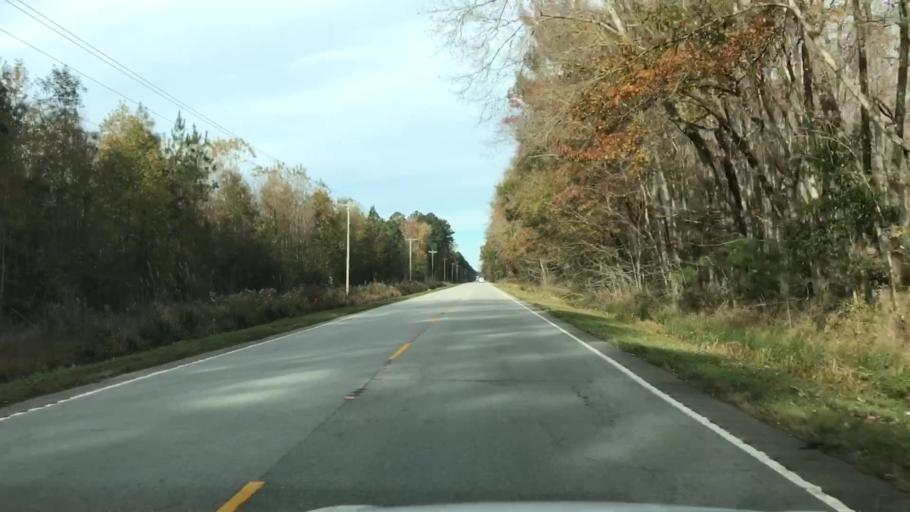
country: US
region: South Carolina
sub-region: Colleton County
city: Walterboro
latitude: 32.8111
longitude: -80.5277
